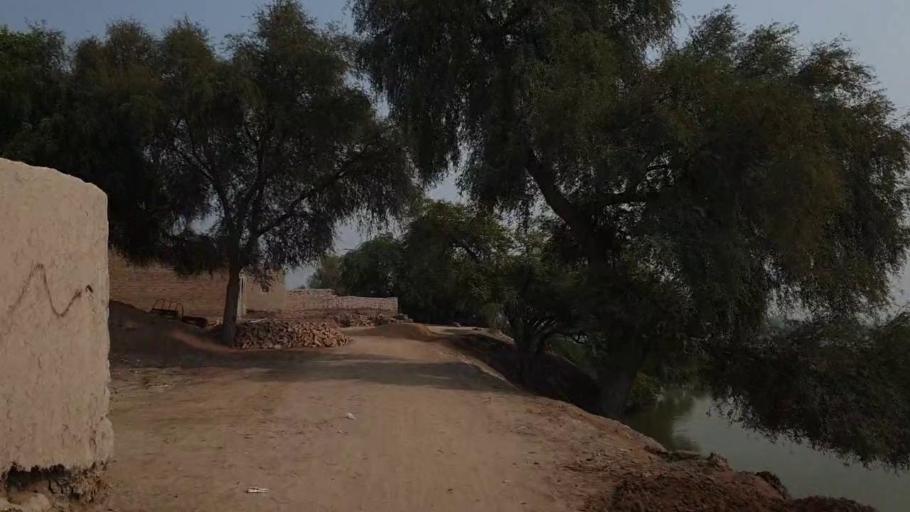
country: PK
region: Sindh
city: Bhan
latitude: 26.5069
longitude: 67.6913
